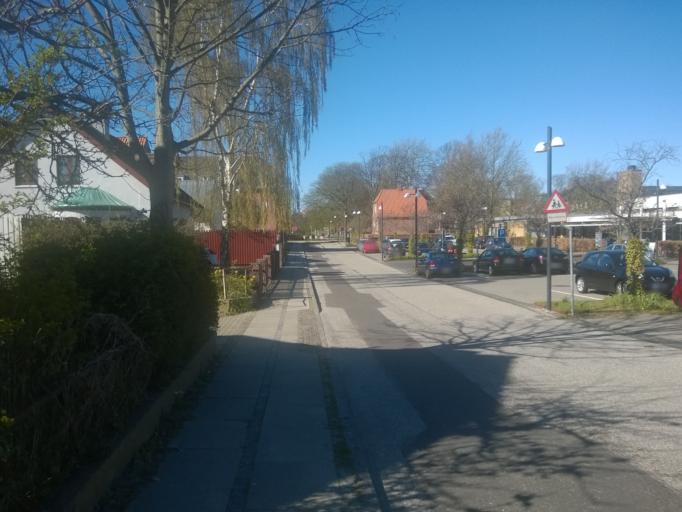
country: DK
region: Capital Region
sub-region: Glostrup Kommune
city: Glostrup
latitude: 55.6633
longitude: 12.3936
